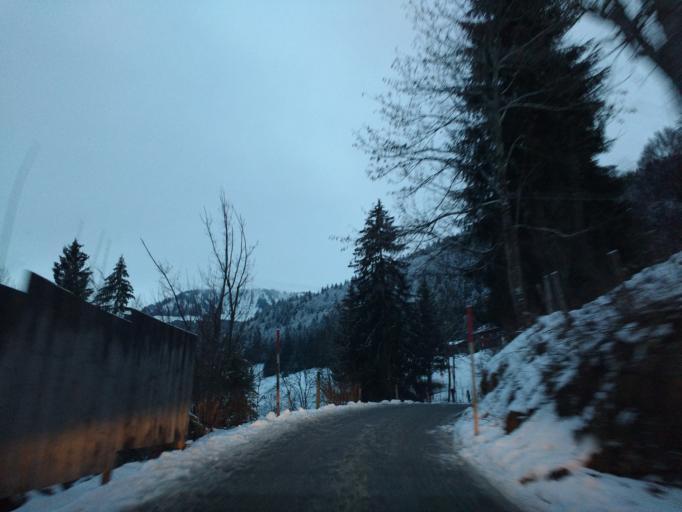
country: DE
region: Bavaria
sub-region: Swabia
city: Obermaiselstein
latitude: 47.4024
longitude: 10.2218
